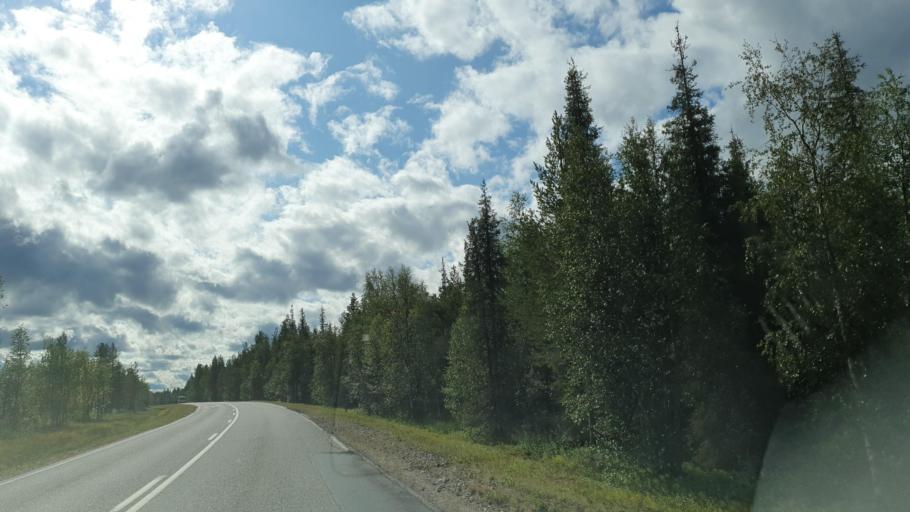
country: FI
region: Lapland
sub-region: Tunturi-Lappi
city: Muonio
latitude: 67.8811
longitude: 24.2090
